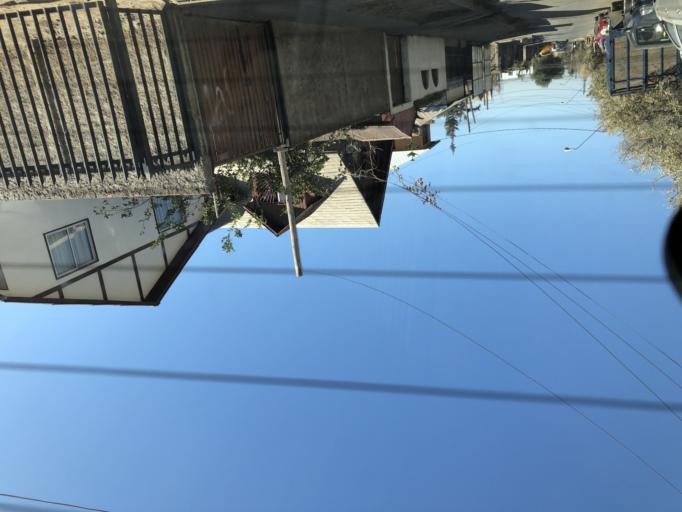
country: CL
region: Santiago Metropolitan
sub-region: Provincia de Cordillera
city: Puente Alto
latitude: -33.6265
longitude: -70.6101
